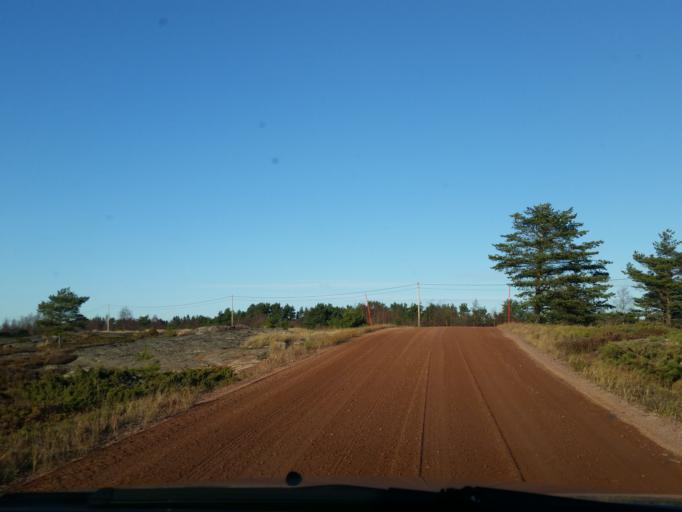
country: AX
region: Alands skaergard
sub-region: Braendoe
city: Braendoe
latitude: 60.4443
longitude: 20.9370
